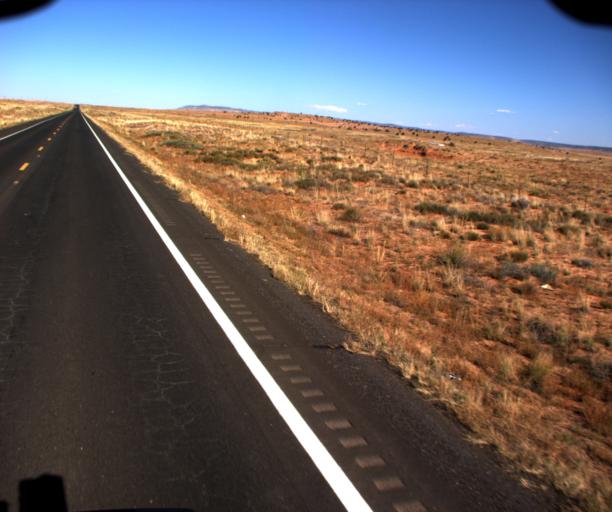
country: US
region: Arizona
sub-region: Coconino County
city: Tuba City
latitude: 36.2806
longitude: -111.0035
